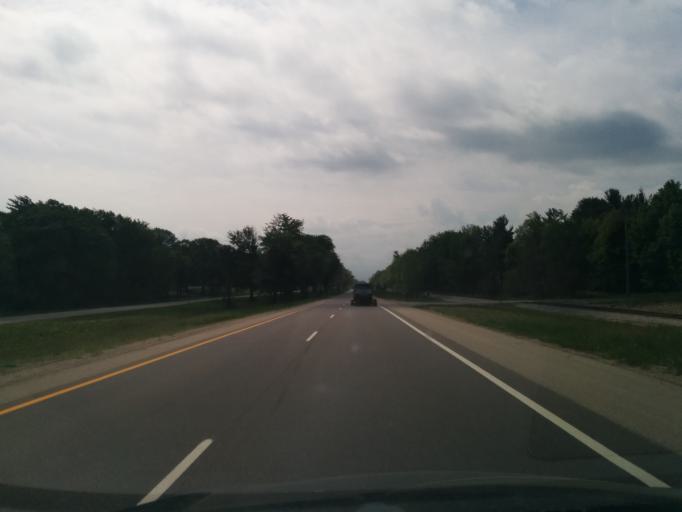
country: US
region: Michigan
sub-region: Ottawa County
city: Grand Haven
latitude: 42.9806
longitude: -86.1889
